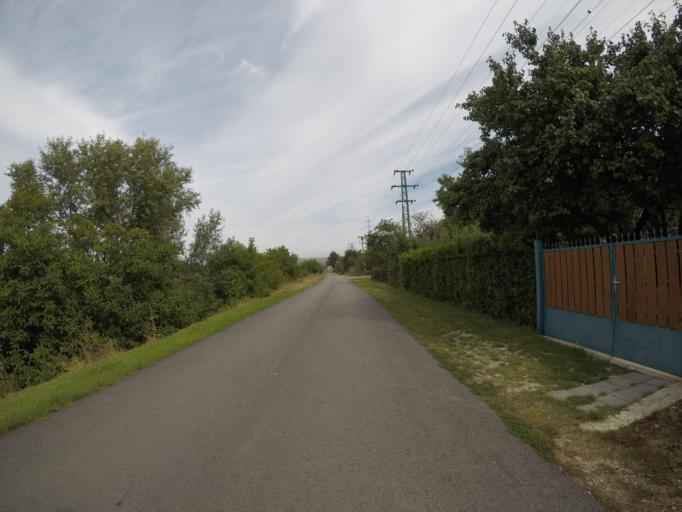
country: SK
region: Trenciansky
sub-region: Okres Nove Mesto nad Vahom
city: Nove Mesto nad Vahom
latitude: 48.7593
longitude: 17.8472
